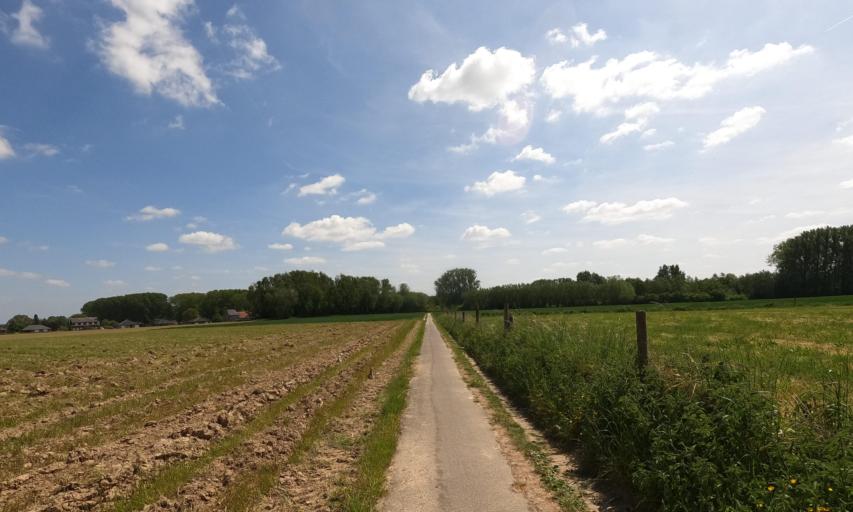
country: BE
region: Flanders
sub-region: Provincie Vlaams-Brabant
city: Opwijk
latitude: 50.9581
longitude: 4.1967
